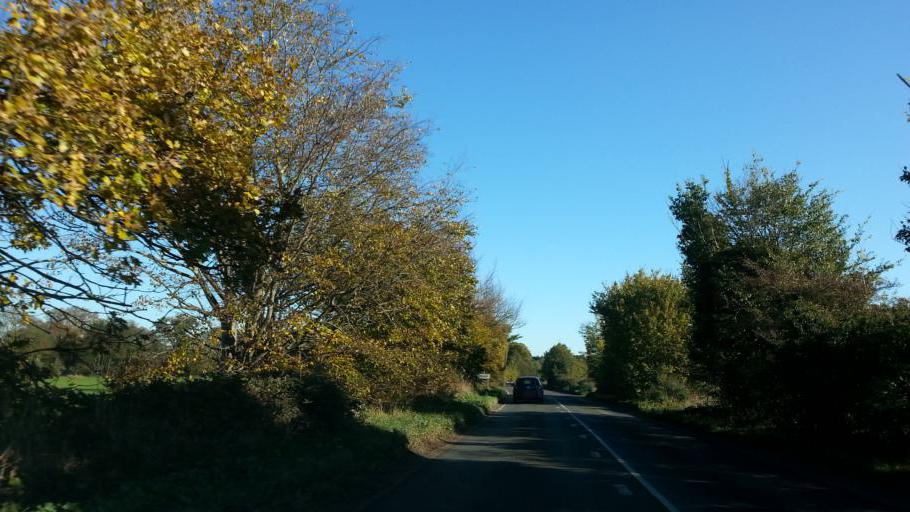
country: GB
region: England
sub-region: Suffolk
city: Wickham Market
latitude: 52.1223
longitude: 1.3948
